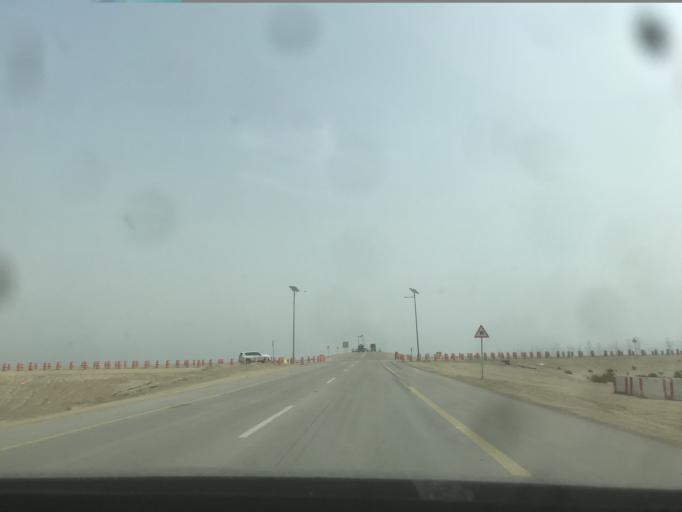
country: SA
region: Eastern Province
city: Abqaiq
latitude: 25.9053
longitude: 50.0150
